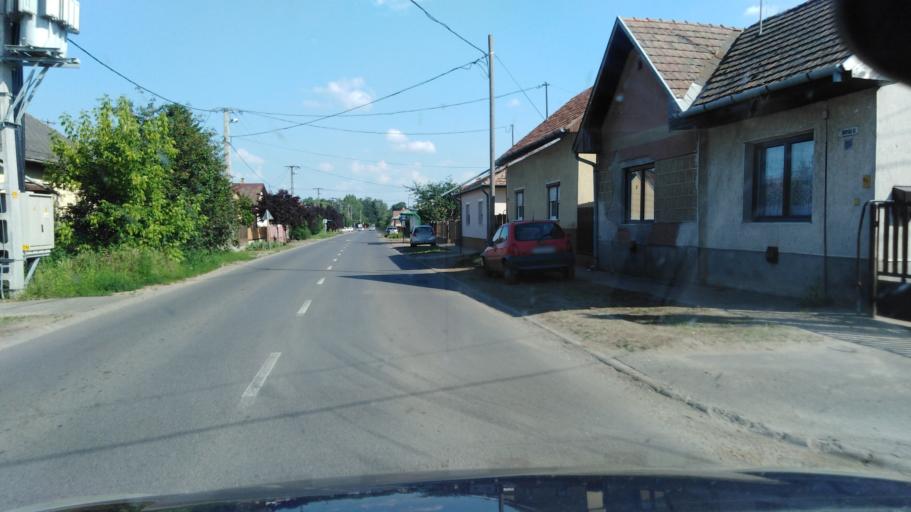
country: HU
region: Szabolcs-Szatmar-Bereg
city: Nyirbator
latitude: 47.8291
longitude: 22.1406
